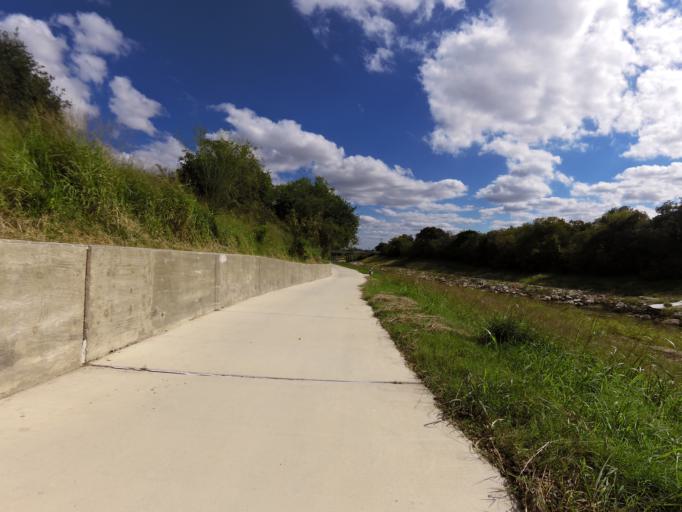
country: US
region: Texas
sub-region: Bexar County
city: San Antonio
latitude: 29.3927
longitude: -98.5022
